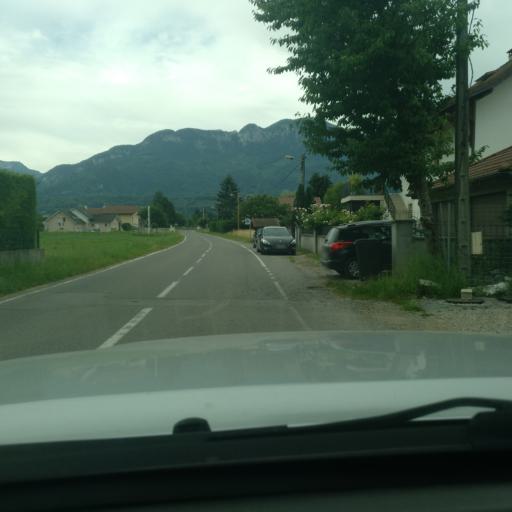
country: FR
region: Rhone-Alpes
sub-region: Departement de la Haute-Savoie
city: Amancy
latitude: 46.0772
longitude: 6.3570
